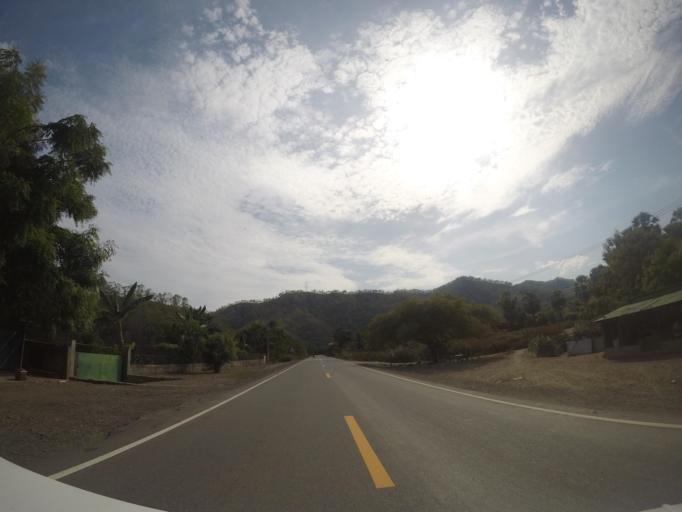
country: ID
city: Metinaro
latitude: -8.5371
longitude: 125.7052
